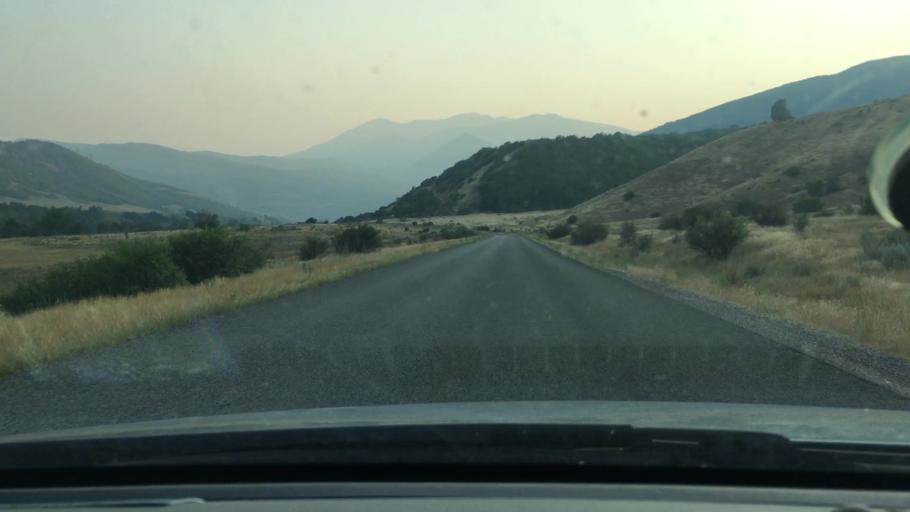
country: US
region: Utah
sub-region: Utah County
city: Mapleton
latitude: 40.0464
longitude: -111.4757
